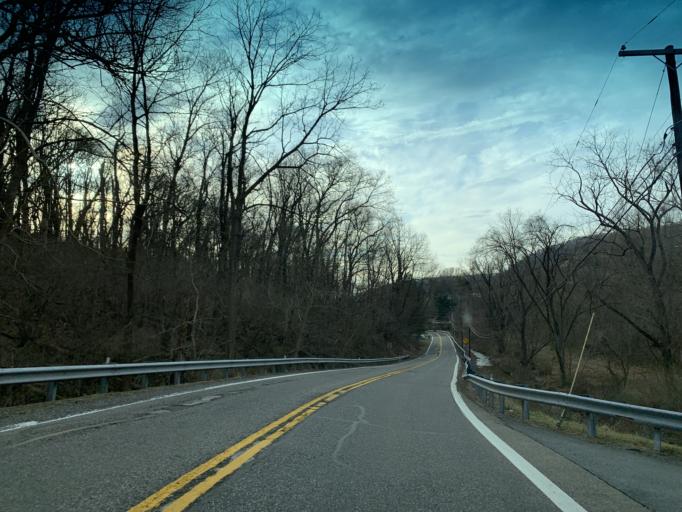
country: US
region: Maryland
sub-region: Frederick County
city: Brunswick
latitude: 39.3282
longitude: -77.6600
